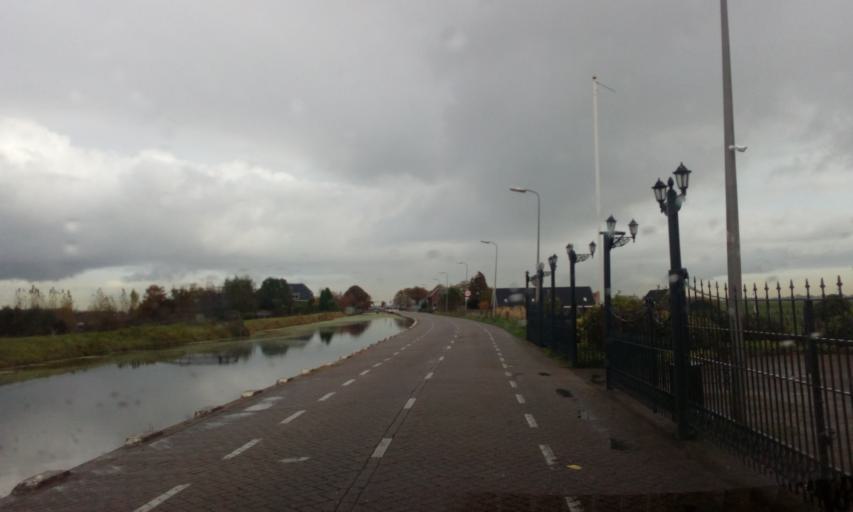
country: NL
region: South Holland
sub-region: Gemeente Voorschoten
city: Voorschoten
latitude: 52.0821
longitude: 4.4232
